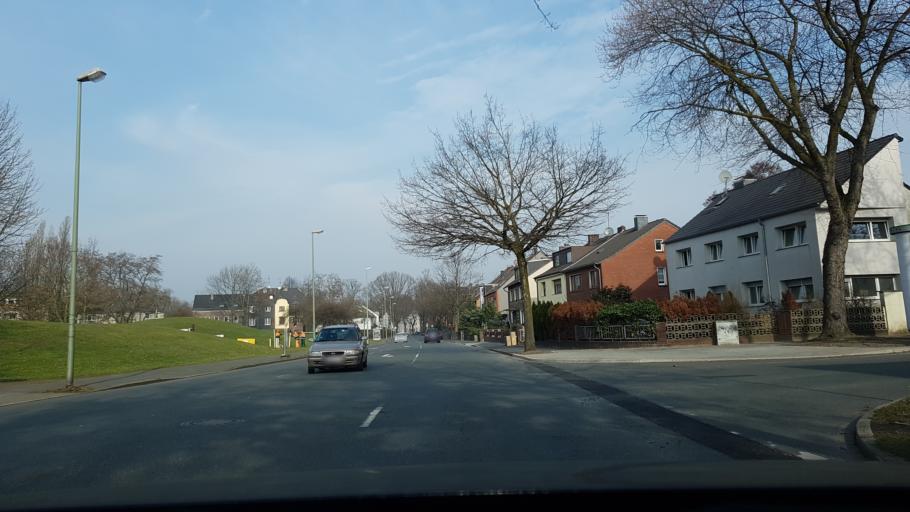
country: DE
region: North Rhine-Westphalia
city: Meiderich
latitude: 51.5015
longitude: 6.7970
